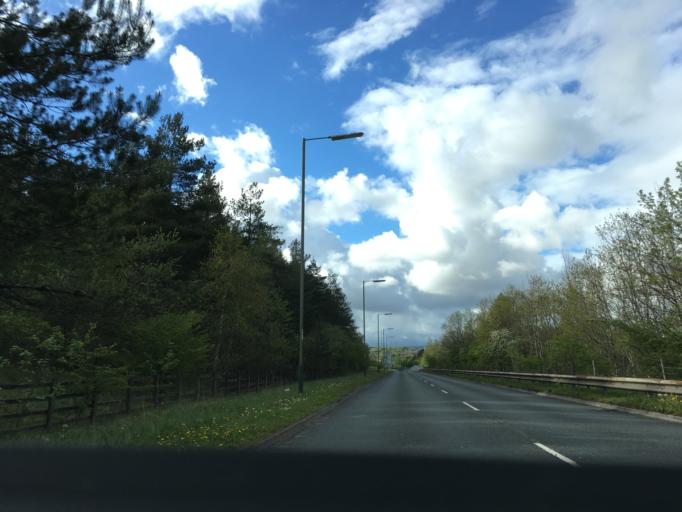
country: GB
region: Wales
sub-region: Caerphilly County Borough
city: Rhymney
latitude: 51.7648
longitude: -3.2935
